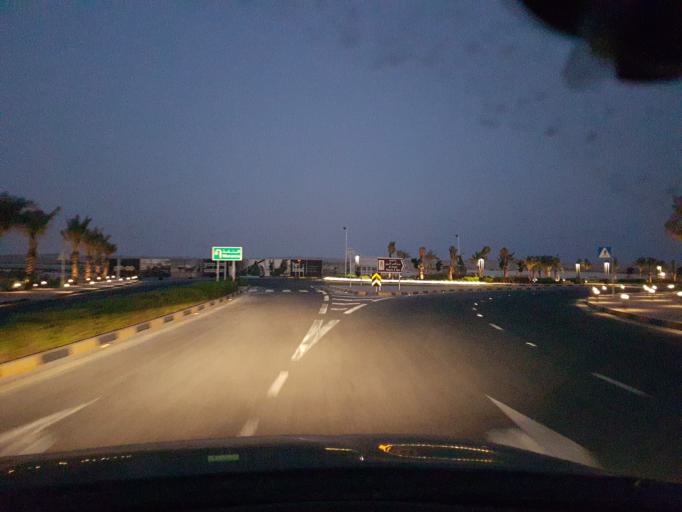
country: BH
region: Central Governorate
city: Dar Kulayb
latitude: 26.0154
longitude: 50.5112
